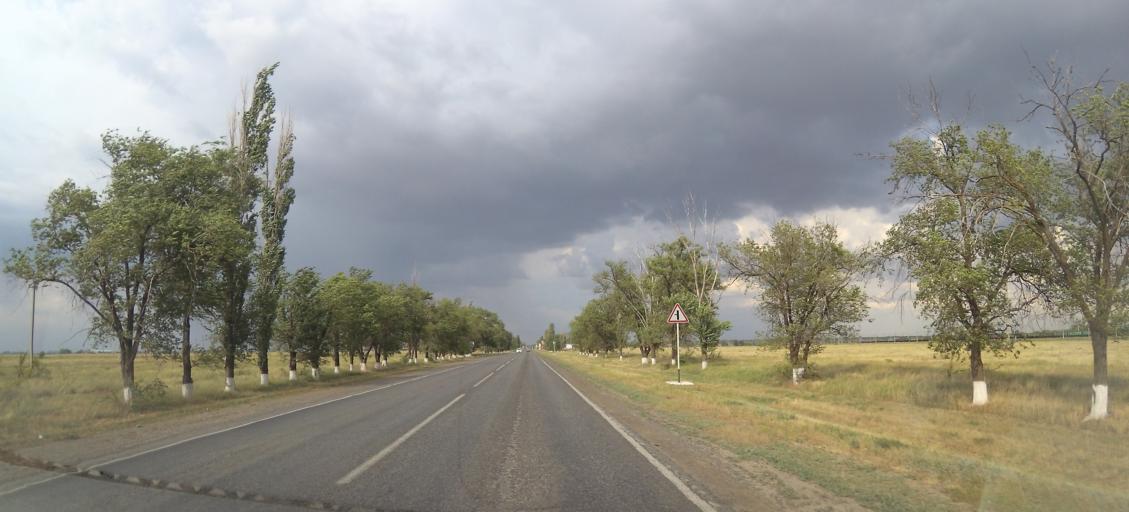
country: RU
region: Rostov
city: Zimovniki
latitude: 47.1369
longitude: 42.4289
